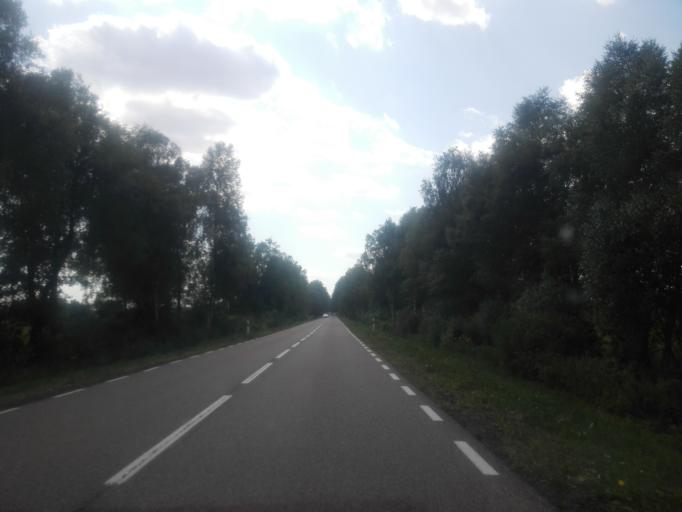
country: PL
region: Podlasie
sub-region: Powiat sejnenski
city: Krasnopol
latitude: 53.9478
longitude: 23.1953
